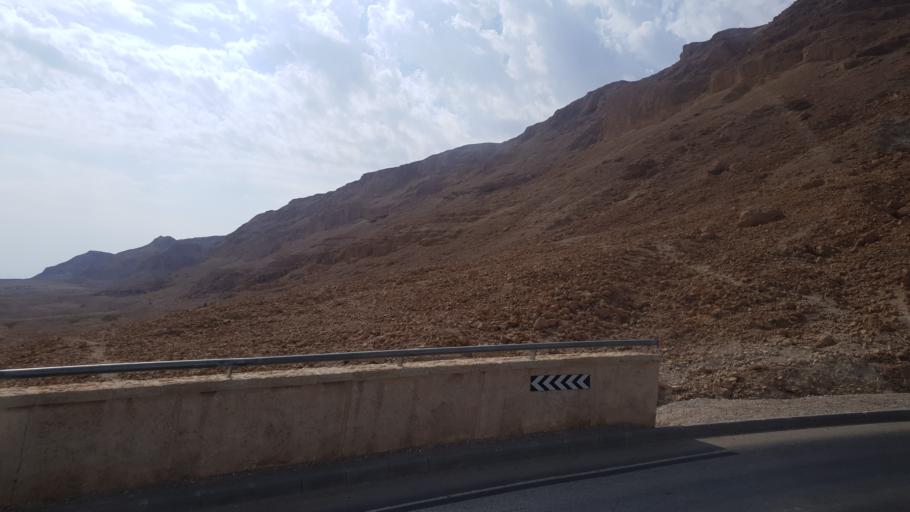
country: IL
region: Southern District
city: `En Boqeq
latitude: 31.3100
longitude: 35.3630
